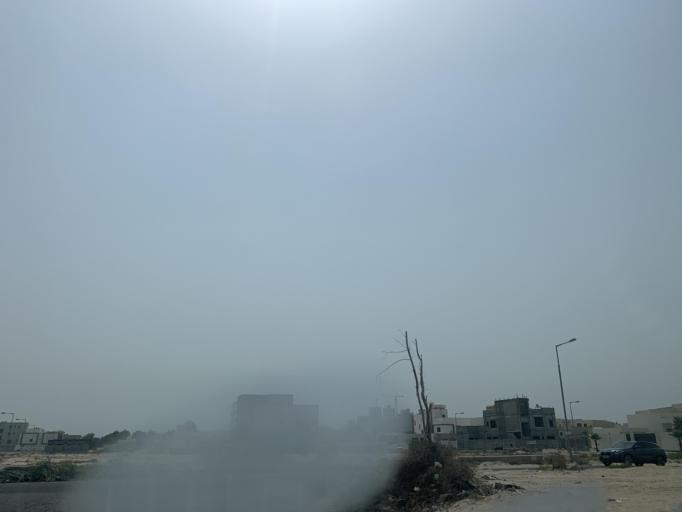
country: BH
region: Manama
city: Jidd Hafs
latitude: 26.2007
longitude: 50.4665
